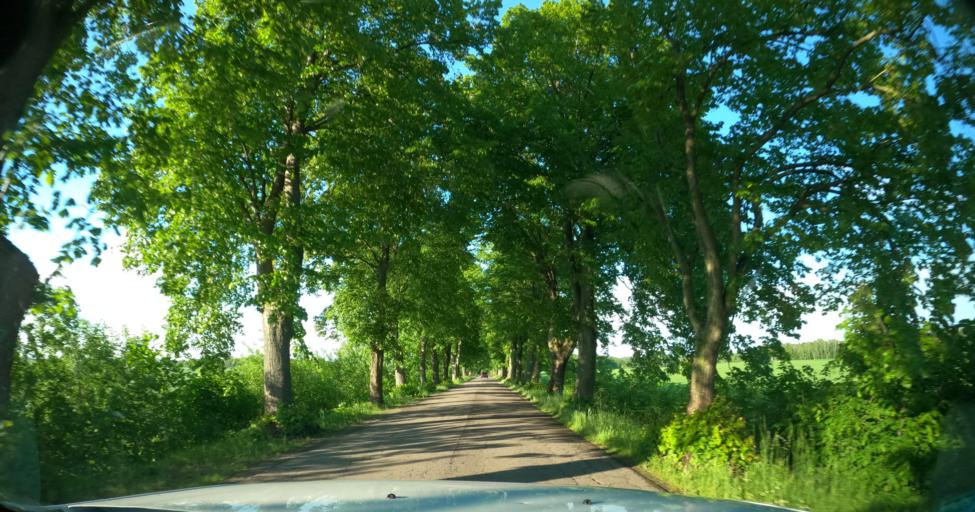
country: PL
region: Warmian-Masurian Voivodeship
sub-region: Powiat braniewski
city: Braniewo
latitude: 54.2758
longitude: 19.8396
